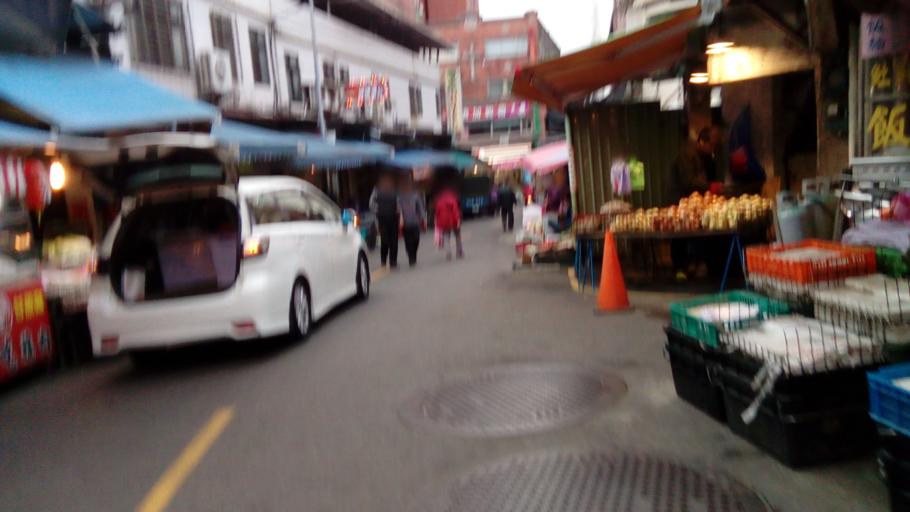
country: TW
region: Taipei
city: Taipei
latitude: 25.1702
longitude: 121.4418
